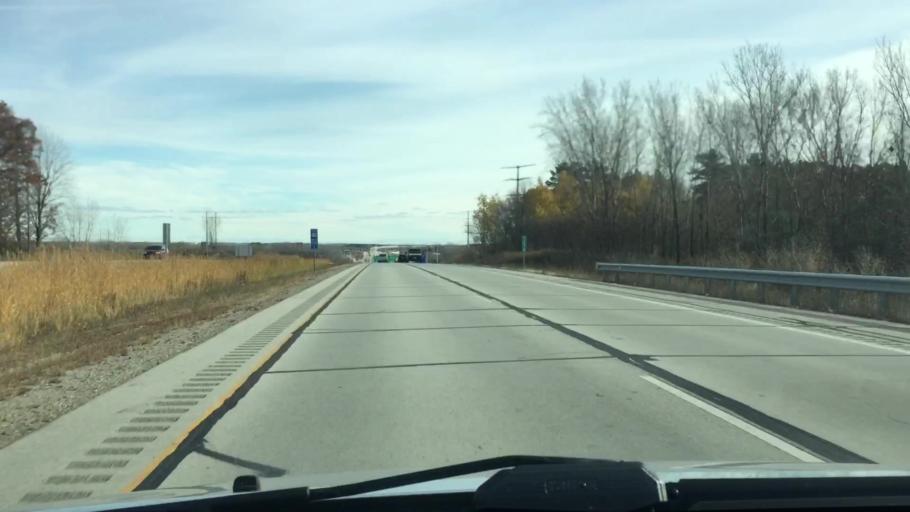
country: US
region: Wisconsin
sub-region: Brown County
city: Howard
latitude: 44.5506
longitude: -88.1068
